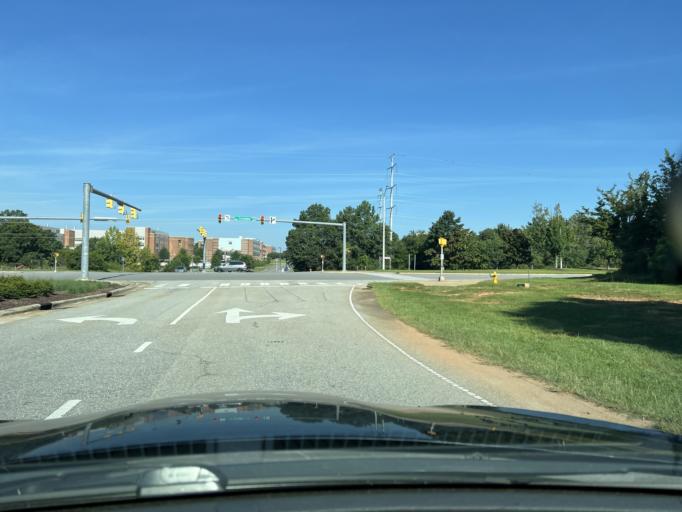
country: US
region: North Carolina
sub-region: Wake County
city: West Raleigh
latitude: 35.7702
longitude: -78.6688
